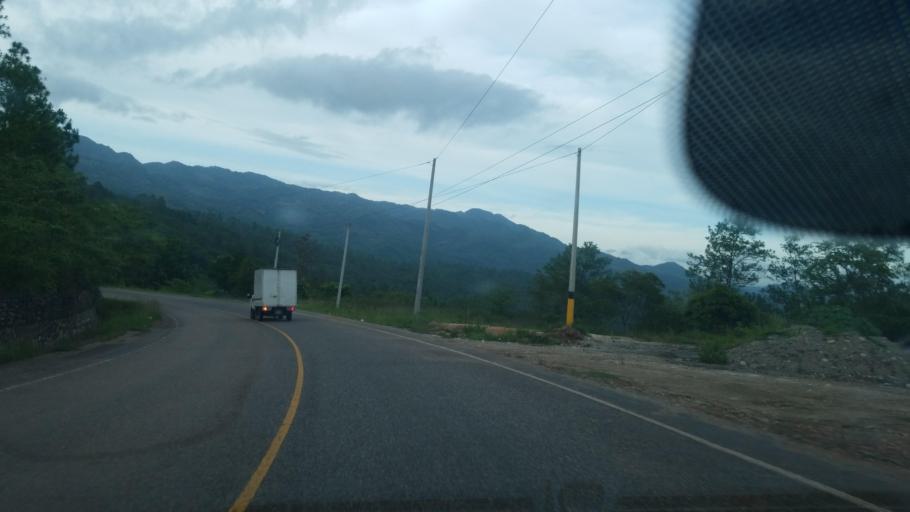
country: HN
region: Santa Barbara
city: Concepcion del Sur
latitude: 14.7960
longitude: -88.1528
